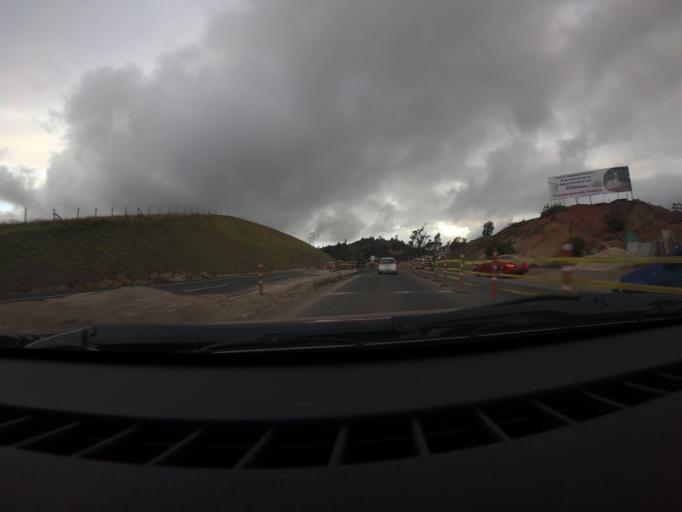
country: CO
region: Boyaca
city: Samaca
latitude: 5.4445
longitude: -73.4359
